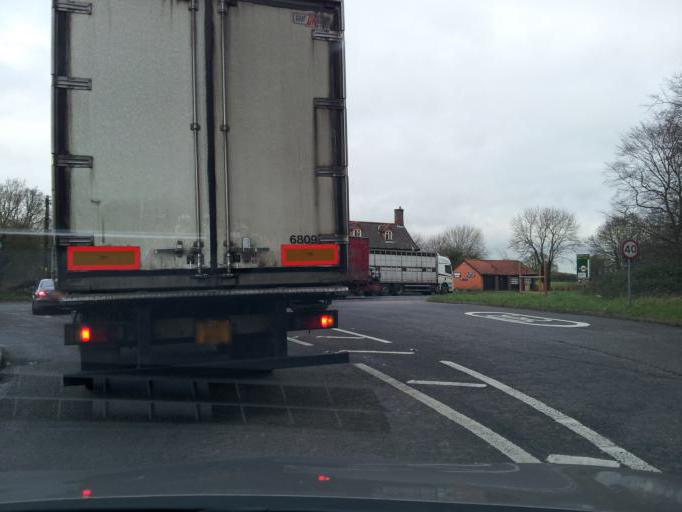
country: GB
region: England
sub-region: Norfolk
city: Diss
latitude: 52.3457
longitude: 1.1334
